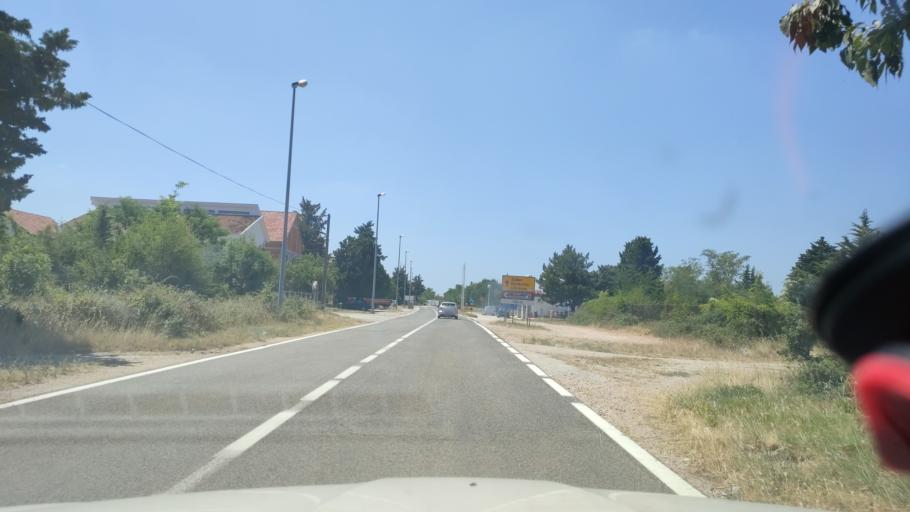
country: HR
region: Sibensko-Kniniska
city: Kistanje
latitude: 43.9853
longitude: 15.9726
